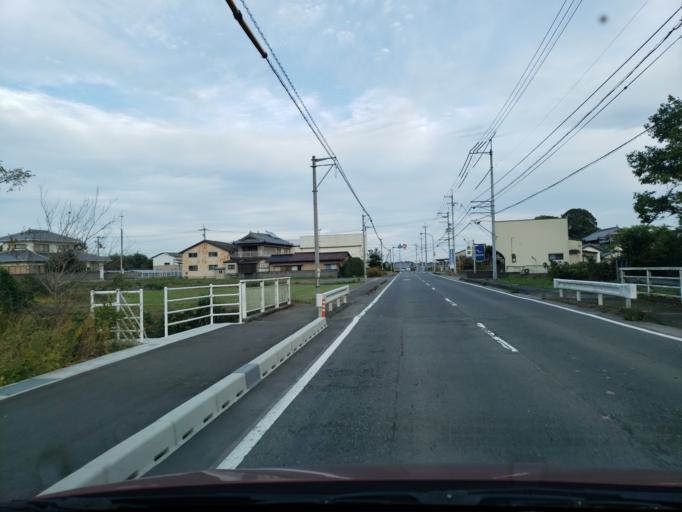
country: JP
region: Tokushima
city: Kamojimacho-jogejima
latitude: 34.0788
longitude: 134.2501
